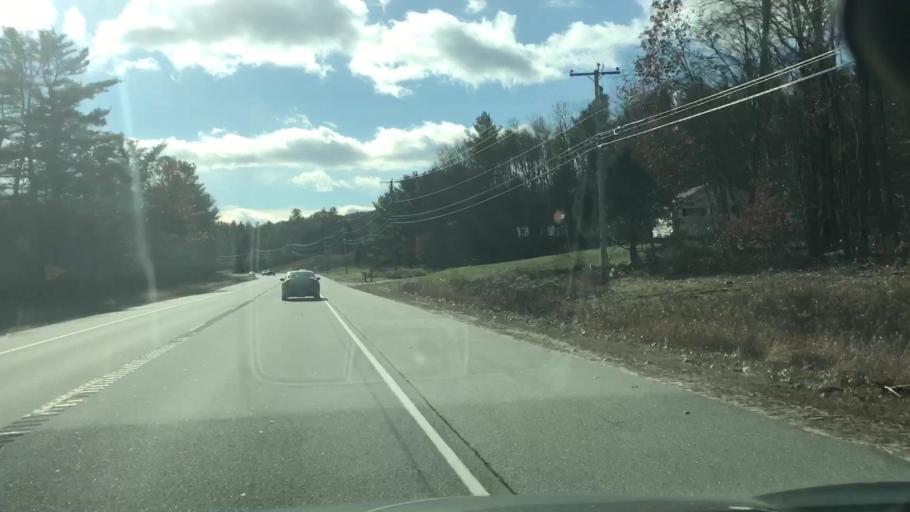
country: US
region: New Hampshire
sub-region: Belknap County
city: Barnstead
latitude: 43.3279
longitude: -71.3037
